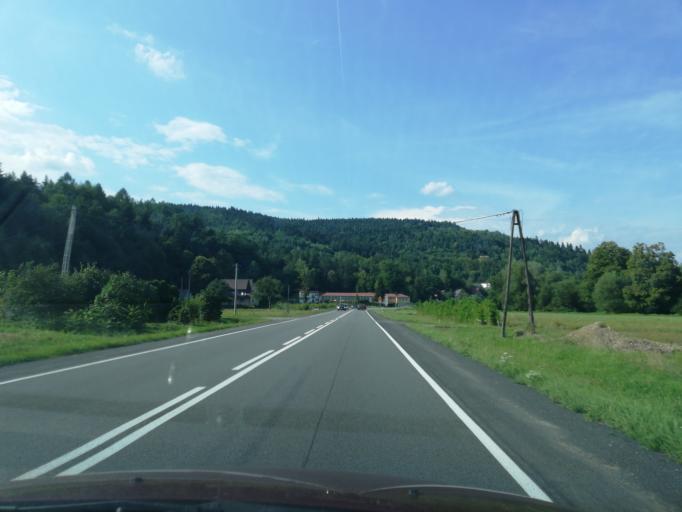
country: PL
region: Lesser Poland Voivodeship
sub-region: Powiat nowosadecki
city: Lososina Dolna
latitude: 49.7764
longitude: 20.6420
